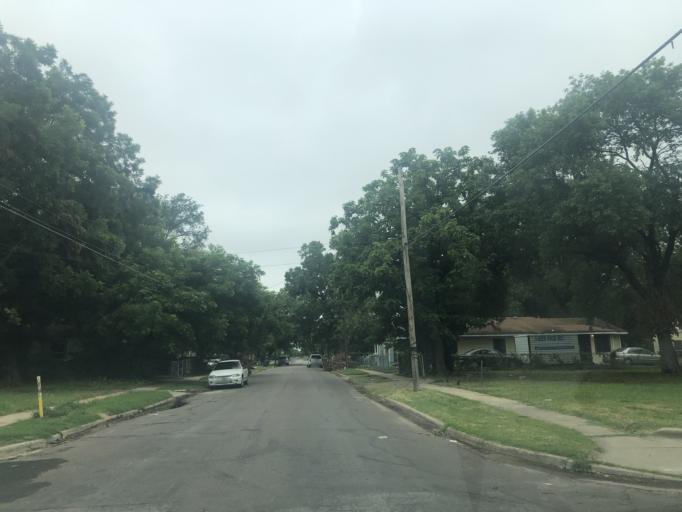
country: US
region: Texas
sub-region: Dallas County
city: Dallas
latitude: 32.7834
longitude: -96.8463
